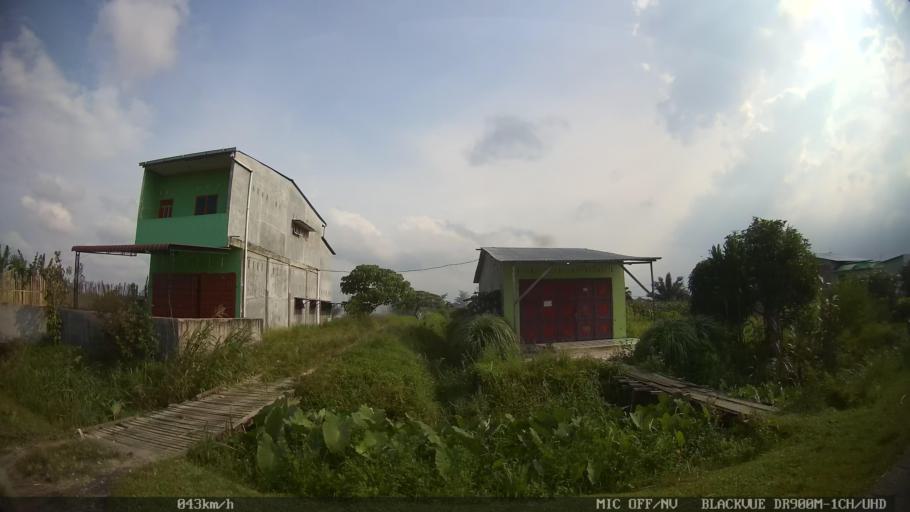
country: ID
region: North Sumatra
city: Medan
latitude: 3.5730
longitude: 98.7658
